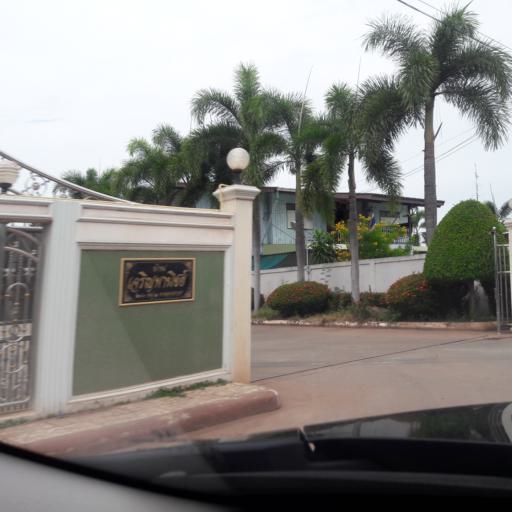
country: TH
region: Ratchaburi
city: Damnoen Saduak
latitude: 13.5587
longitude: 99.9612
